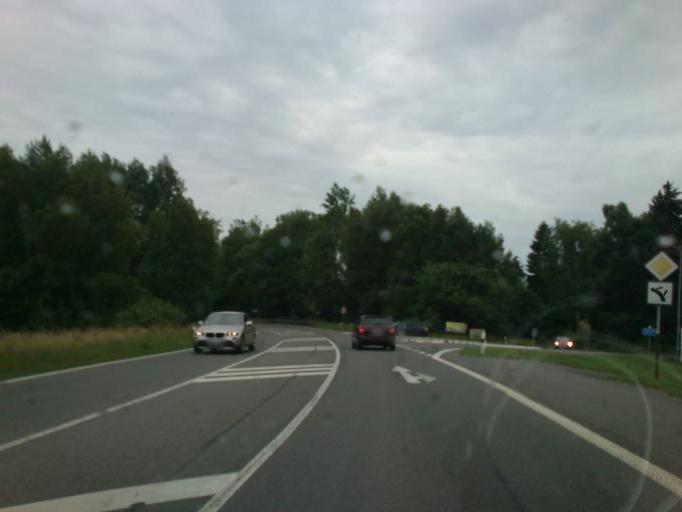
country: CZ
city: Doksy
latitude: 50.5424
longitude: 14.6732
